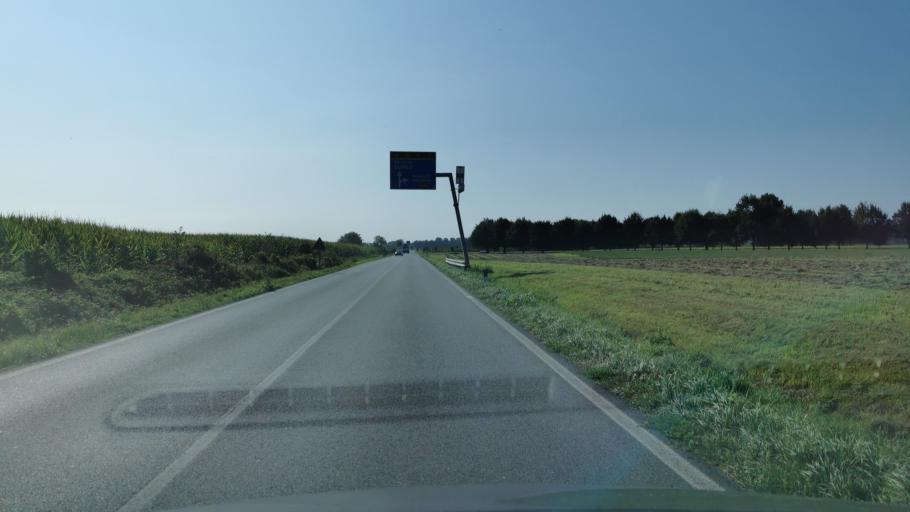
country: IT
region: Piedmont
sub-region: Provincia di Cuneo
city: Carde
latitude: 44.7220
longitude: 7.4387
